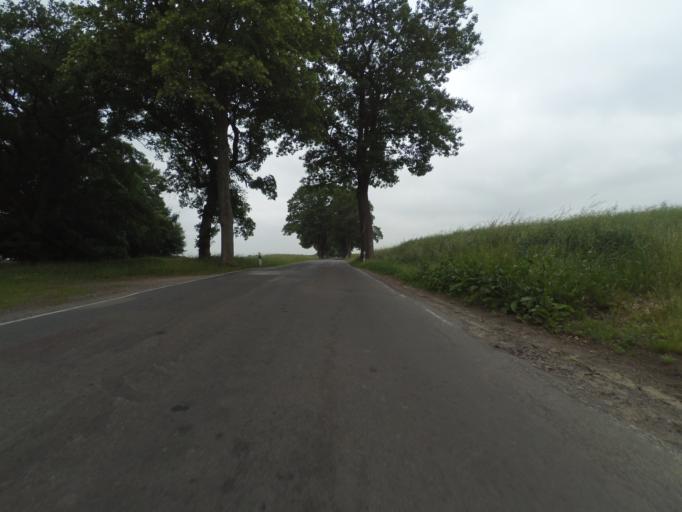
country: DE
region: Mecklenburg-Vorpommern
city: Lubz
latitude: 53.4867
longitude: 11.9763
